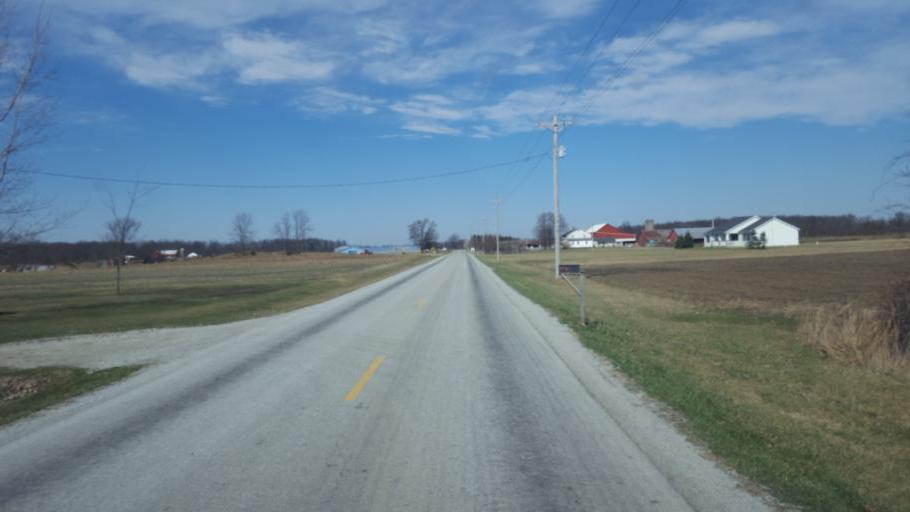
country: US
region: Ohio
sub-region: Hardin County
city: Kenton
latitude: 40.6040
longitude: -83.5036
